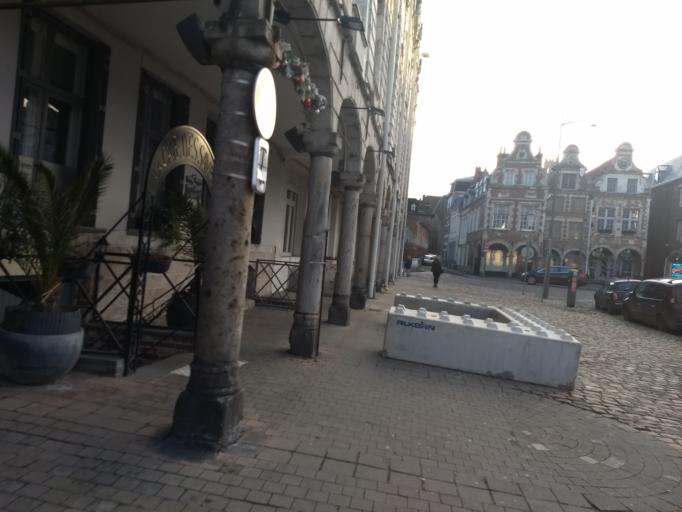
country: FR
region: Nord-Pas-de-Calais
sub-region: Departement du Pas-de-Calais
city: Arras
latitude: 50.2918
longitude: 2.7806
